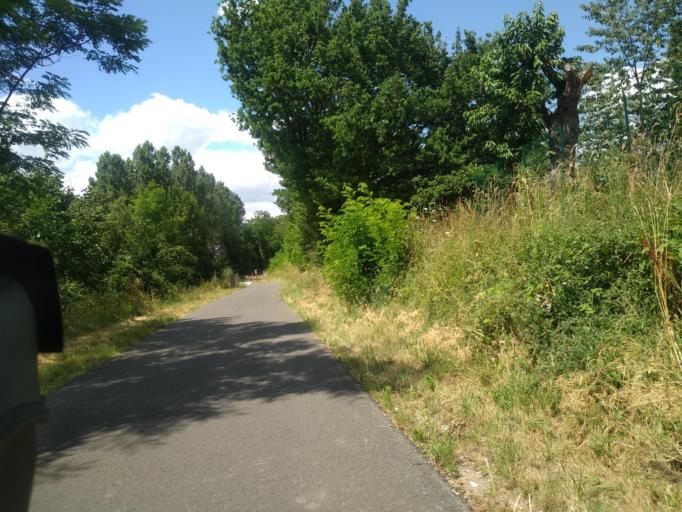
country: FR
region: Rhone-Alpes
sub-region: Departement de la Loire
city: Briennon
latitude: 46.1861
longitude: 4.0873
